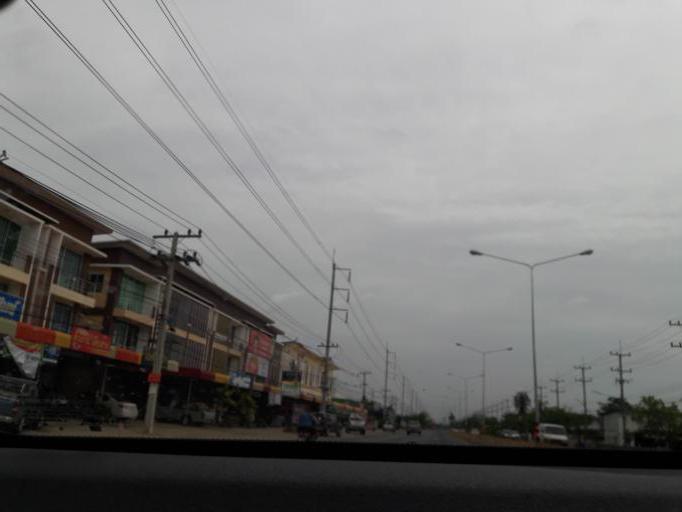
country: TH
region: Ratchaburi
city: Damnoen Saduak
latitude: 13.5758
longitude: 99.9697
